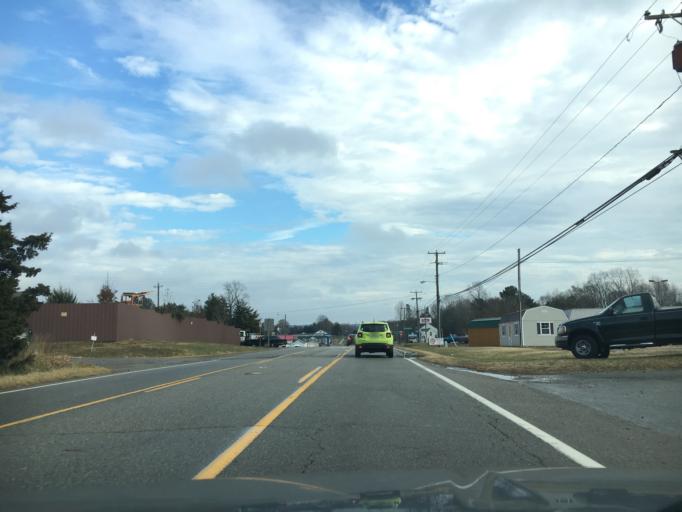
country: US
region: Virginia
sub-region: Prince Edward County
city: Farmville
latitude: 37.3156
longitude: -78.4399
